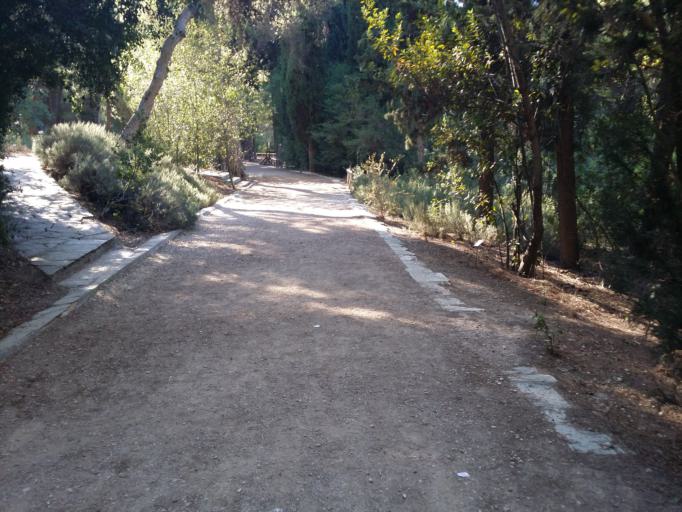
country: GR
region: Attica
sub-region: Nomarchia Athinas
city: Chaidari
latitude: 38.0108
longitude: 23.6435
